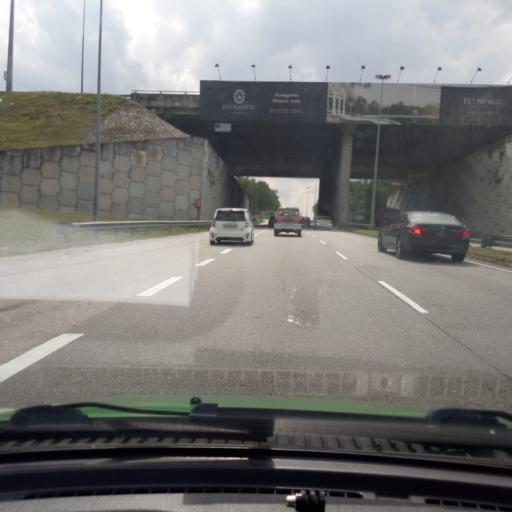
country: MY
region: Selangor
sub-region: Hulu Langat
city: Semenyih
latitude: 2.9855
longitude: 101.8281
